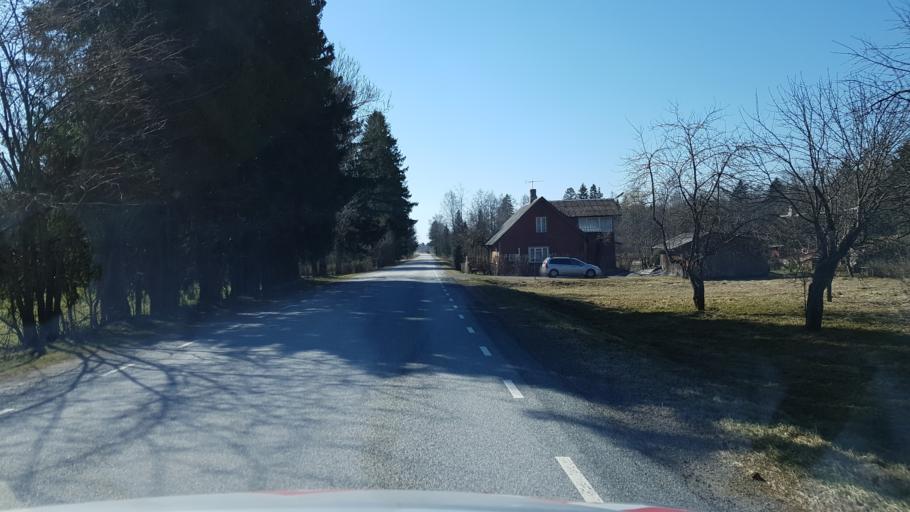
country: EE
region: Ida-Virumaa
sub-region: Kohtla-Nomme vald
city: Kohtla-Nomme
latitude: 59.3017
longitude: 27.2381
